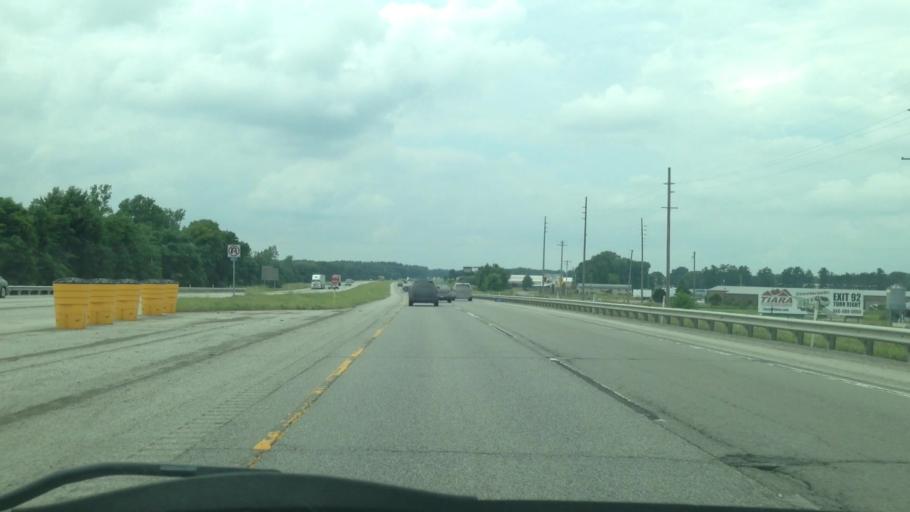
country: US
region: Indiana
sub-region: Elkhart County
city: Middlebury
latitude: 41.7415
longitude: -85.7299
